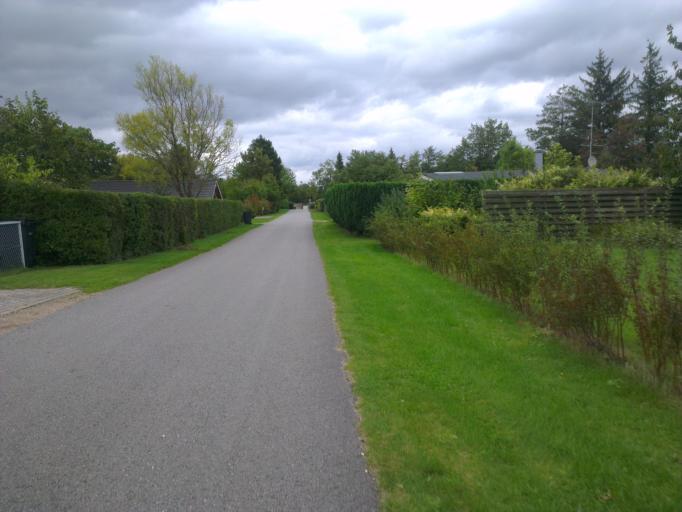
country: DK
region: Capital Region
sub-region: Frederikssund Kommune
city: Jaegerspris
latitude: 55.8317
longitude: 11.9667
